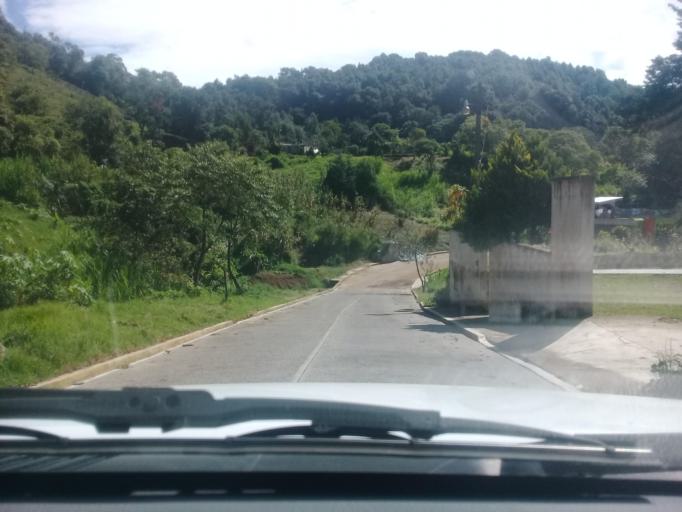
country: MX
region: Veracruz
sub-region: Tlalnelhuayocan
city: Otilpan
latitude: 19.5681
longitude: -96.9881
